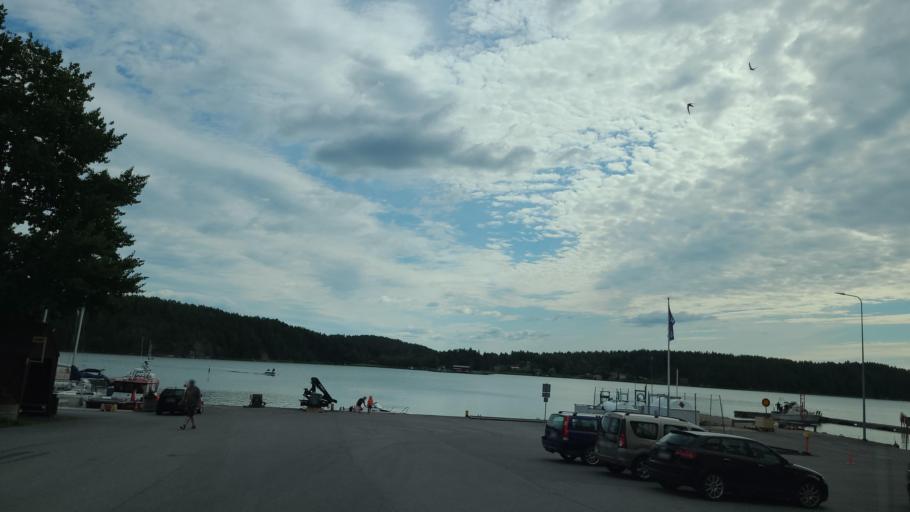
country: FI
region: Varsinais-Suomi
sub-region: Turku
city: Rymaettylae
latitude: 60.3458
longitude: 21.9565
